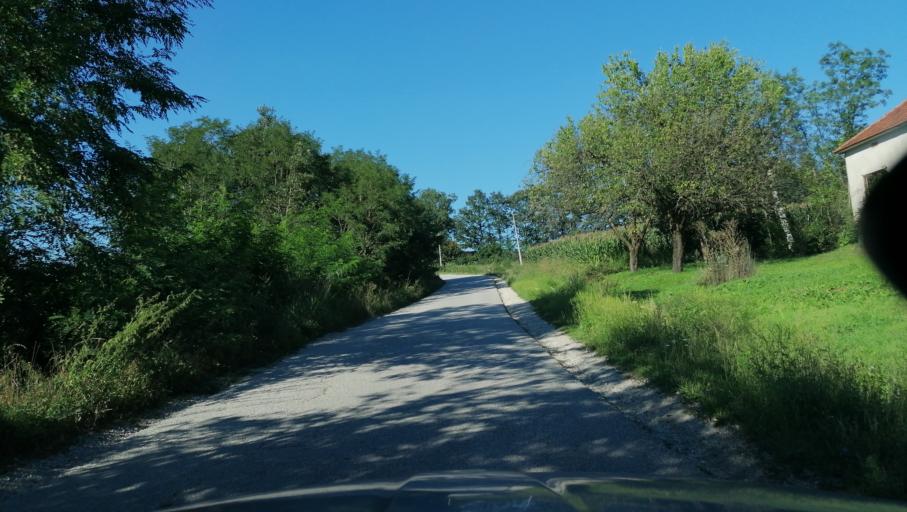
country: RS
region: Central Serbia
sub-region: Sumadijski Okrug
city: Knic
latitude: 43.8663
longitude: 20.6048
